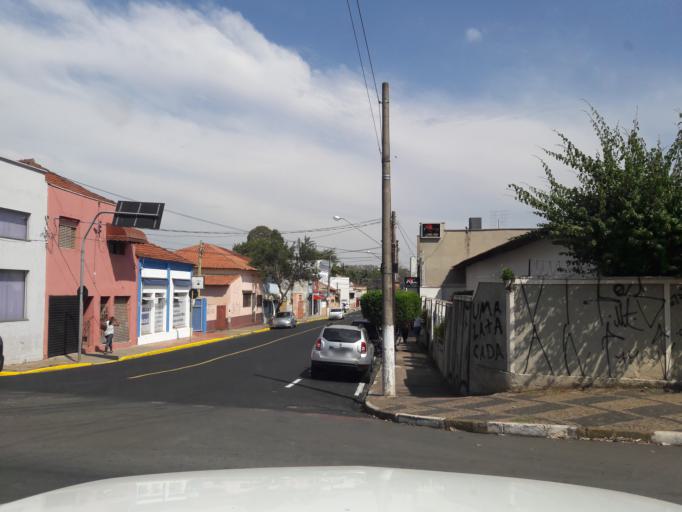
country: BR
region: Sao Paulo
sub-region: Moji-Guacu
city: Mogi-Gaucu
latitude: -22.3699
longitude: -46.9392
